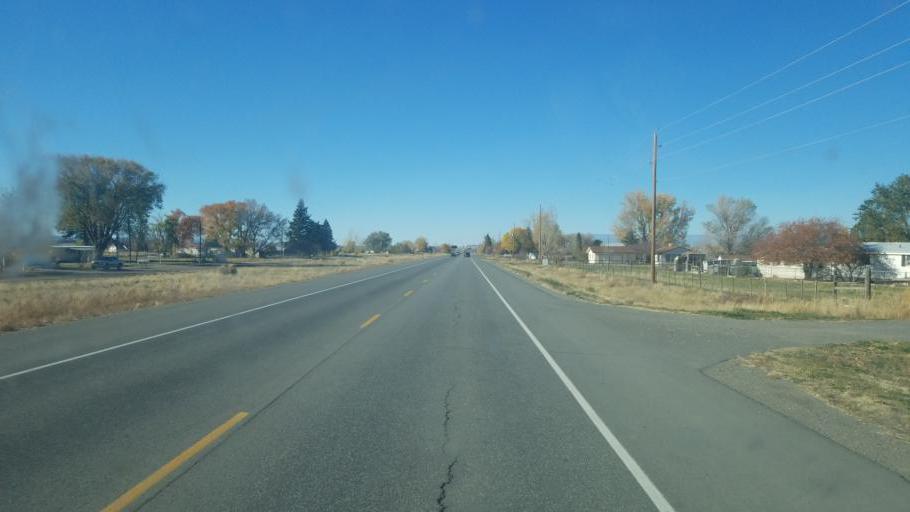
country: US
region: Colorado
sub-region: Montrose County
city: Montrose
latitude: 38.4120
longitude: -107.8483
